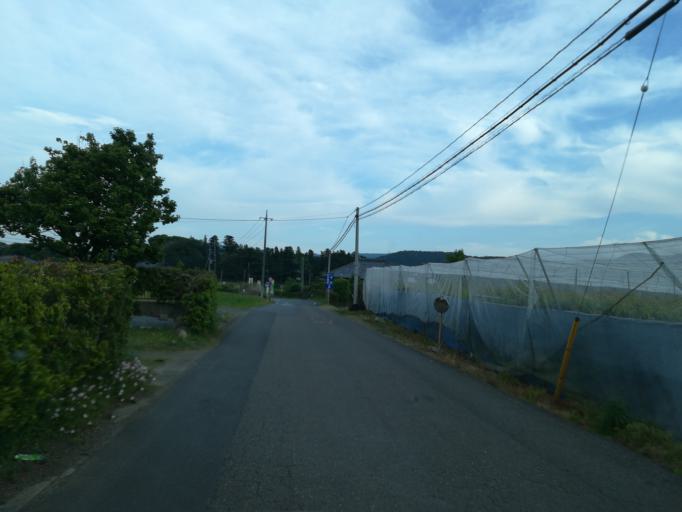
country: JP
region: Ibaraki
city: Tsukuba
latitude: 36.2259
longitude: 140.1506
